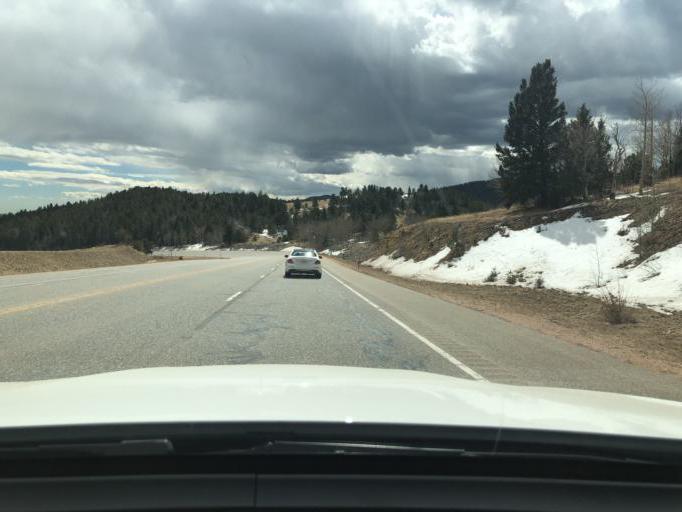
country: US
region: Colorado
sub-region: Gilpin County
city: Central City
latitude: 39.7869
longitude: -105.4965
